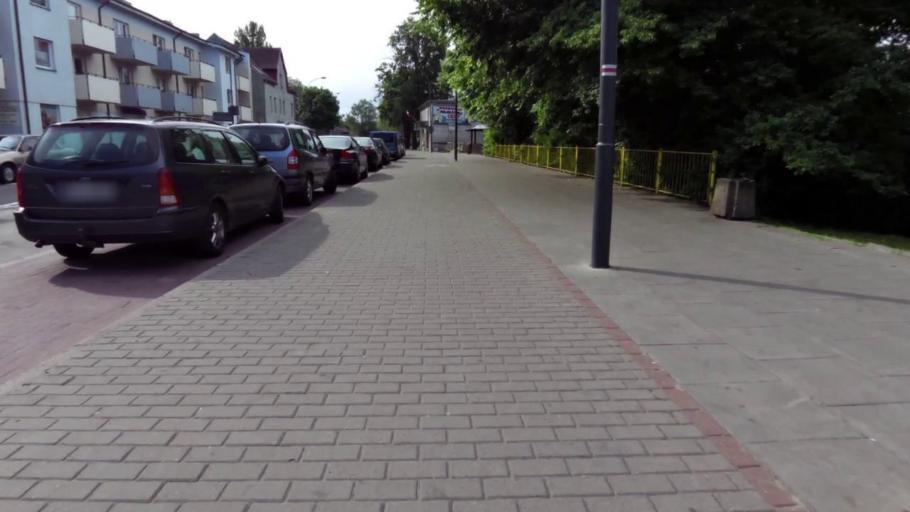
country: PL
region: West Pomeranian Voivodeship
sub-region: Swinoujscie
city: Swinoujscie
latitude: 53.9055
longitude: 14.2695
